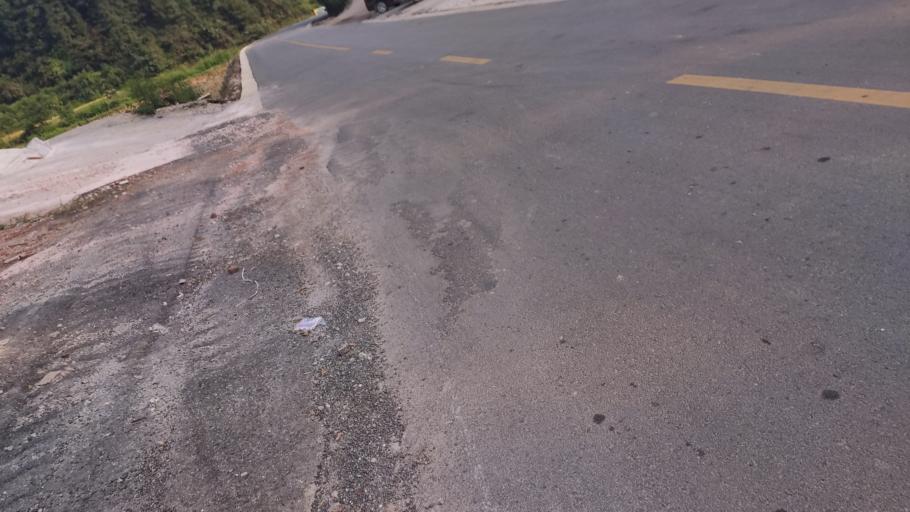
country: CN
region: Guizhou Sheng
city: Zhongchao
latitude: 26.1515
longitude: 109.2064
